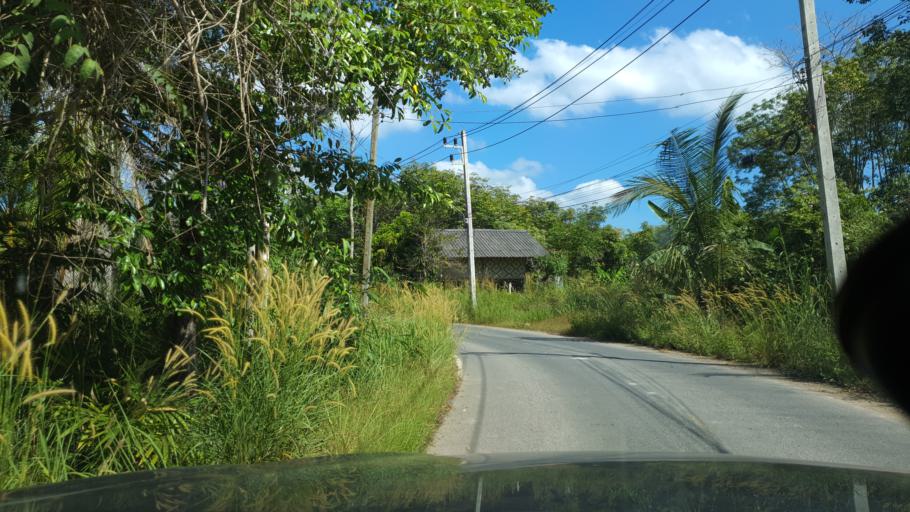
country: TH
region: Phangnga
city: Ban Ao Nang
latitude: 8.0303
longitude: 98.8572
